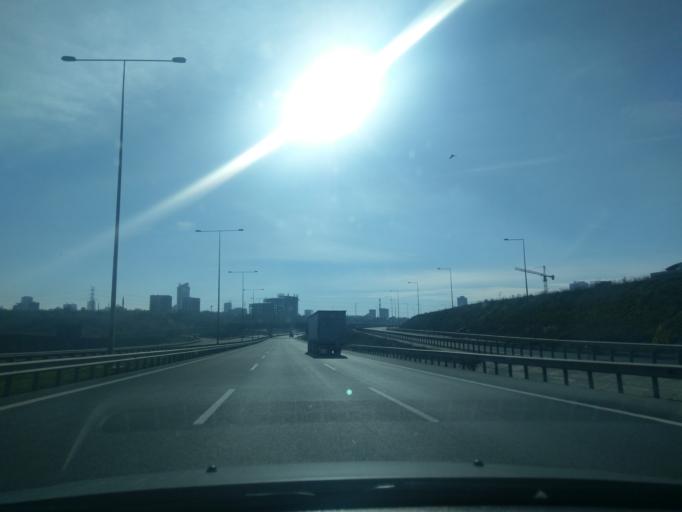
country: TR
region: Istanbul
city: Basaksehir
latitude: 41.0781
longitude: 28.8141
